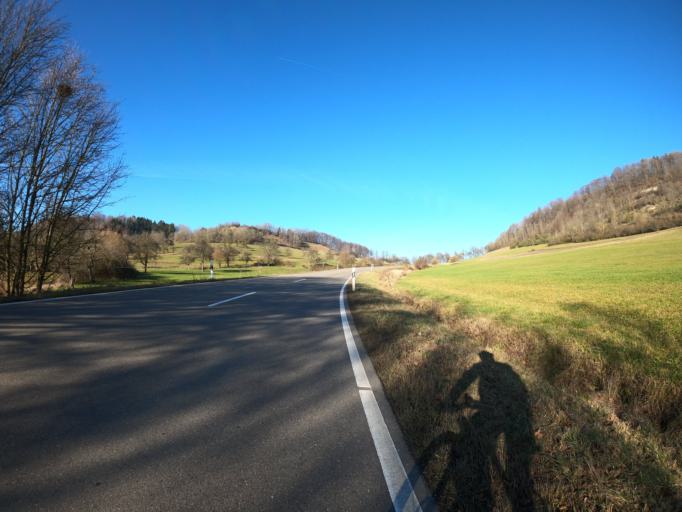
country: DE
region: Baden-Wuerttemberg
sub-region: Regierungsbezirk Stuttgart
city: Gammelshausen
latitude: 48.6233
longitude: 9.6747
